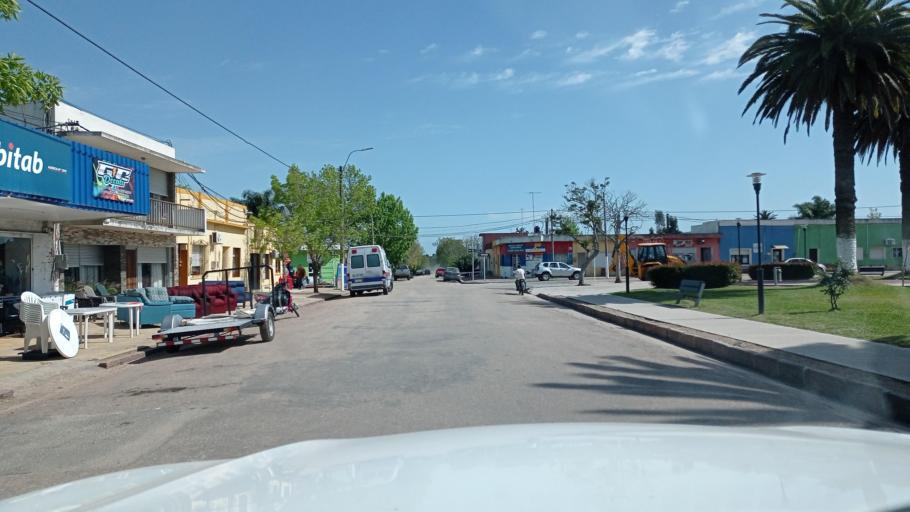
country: UY
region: Canelones
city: Santa Rosa
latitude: -34.4986
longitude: -56.0415
